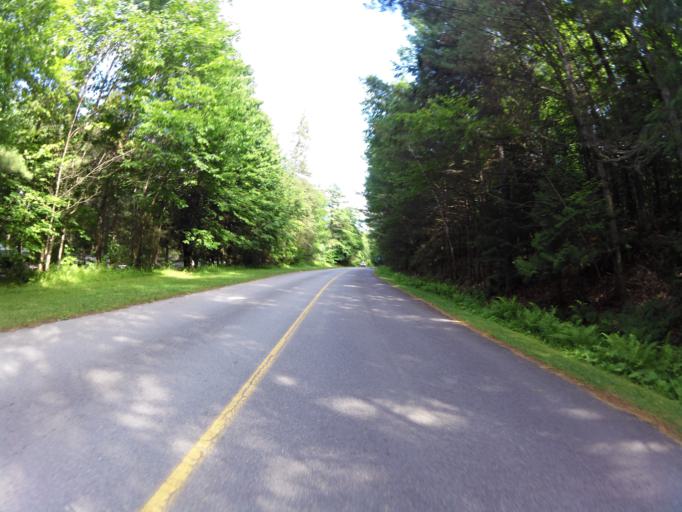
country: CA
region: Quebec
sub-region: Outaouais
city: Wakefield
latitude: 45.6026
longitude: -76.0093
